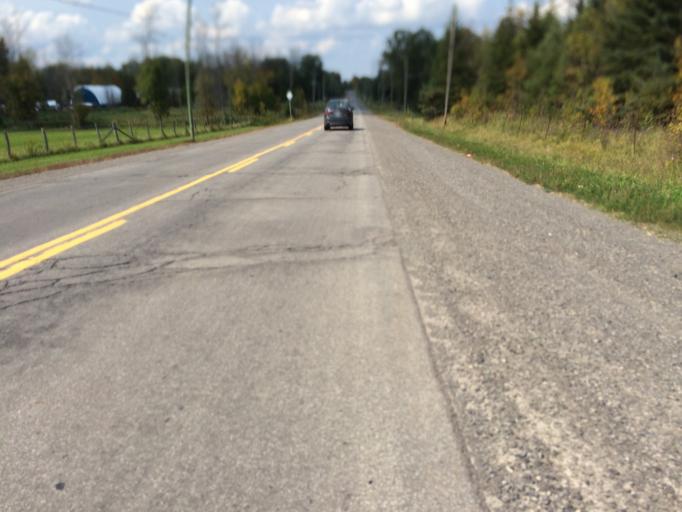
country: CA
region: Ontario
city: Bells Corners
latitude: 45.1988
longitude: -75.6453
